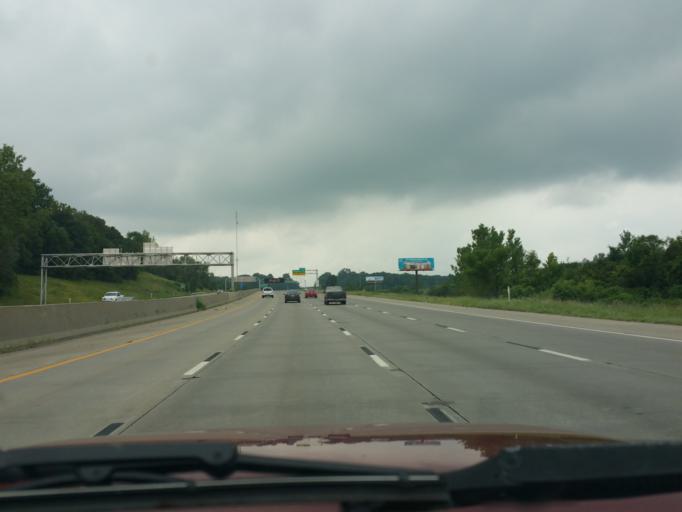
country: US
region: Kansas
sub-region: Johnson County
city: Shawnee
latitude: 39.0718
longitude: -94.6805
